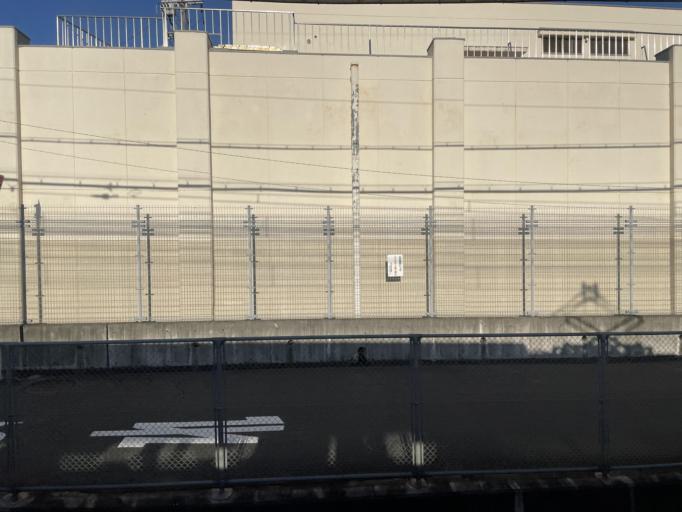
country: JP
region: Osaka
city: Kashihara
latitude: 34.5661
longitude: 135.6197
